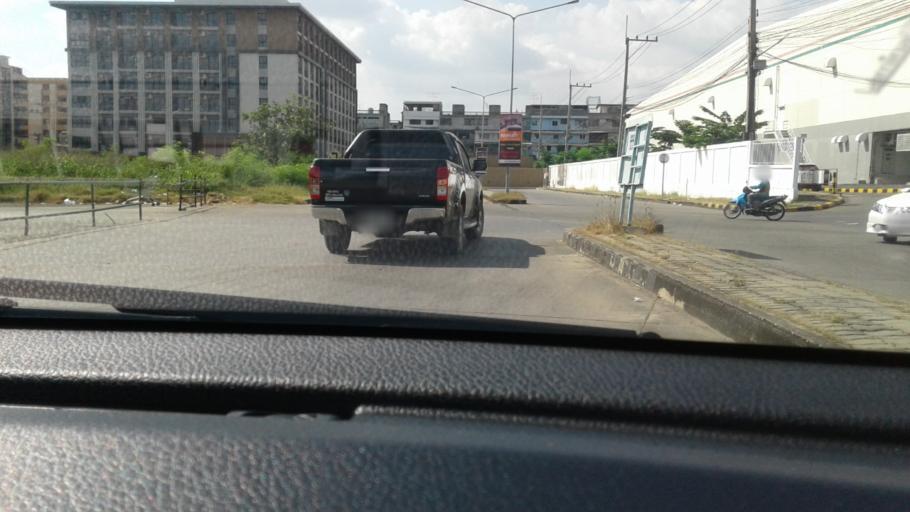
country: TH
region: Phra Nakhon Si Ayutthaya
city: Ban Bang Kadi Pathum Thani
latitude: 13.9929
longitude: 100.6135
